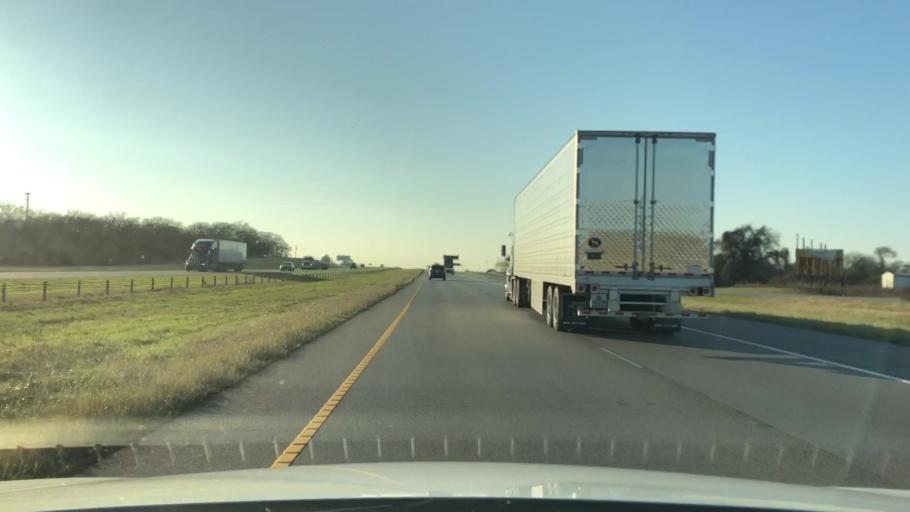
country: US
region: Texas
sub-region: Caldwell County
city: Luling
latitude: 29.6539
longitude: -97.5611
